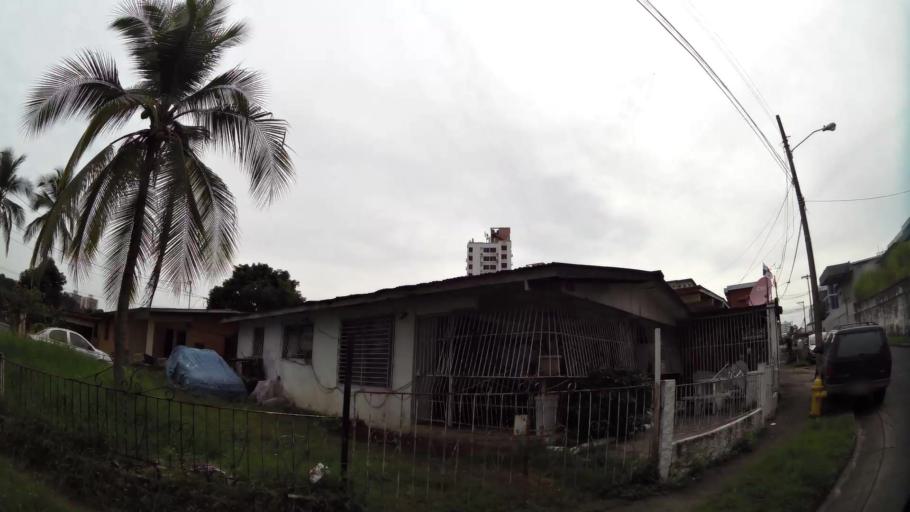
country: PA
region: Panama
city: Panama
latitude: 9.0245
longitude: -79.5224
